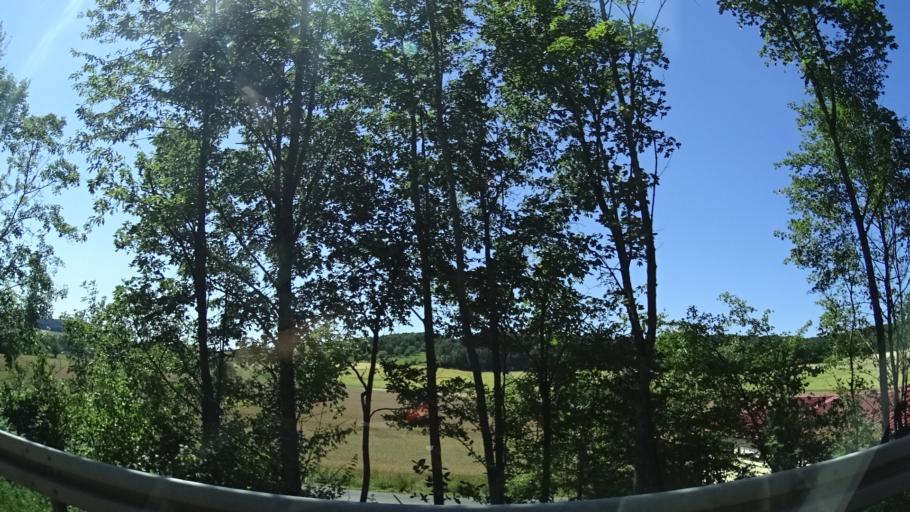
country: DE
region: Bavaria
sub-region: Regierungsbezirk Unterfranken
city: Neubrunn
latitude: 49.7369
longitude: 9.6796
